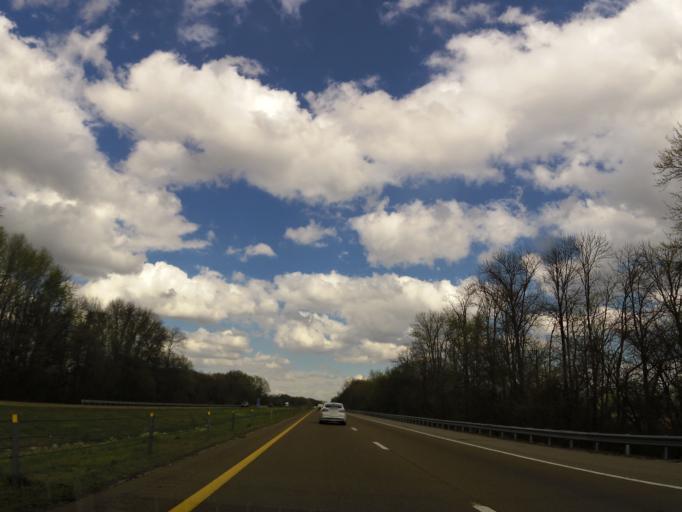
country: US
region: Tennessee
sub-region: Crockett County
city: Bells
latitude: 35.6068
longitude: -89.0296
